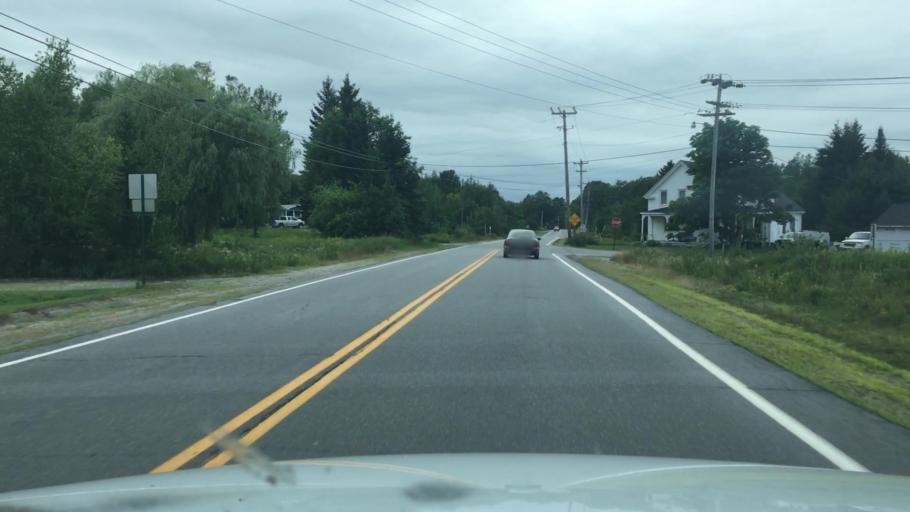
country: US
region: Maine
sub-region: Washington County
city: Cherryfield
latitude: 44.6036
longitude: -67.9387
